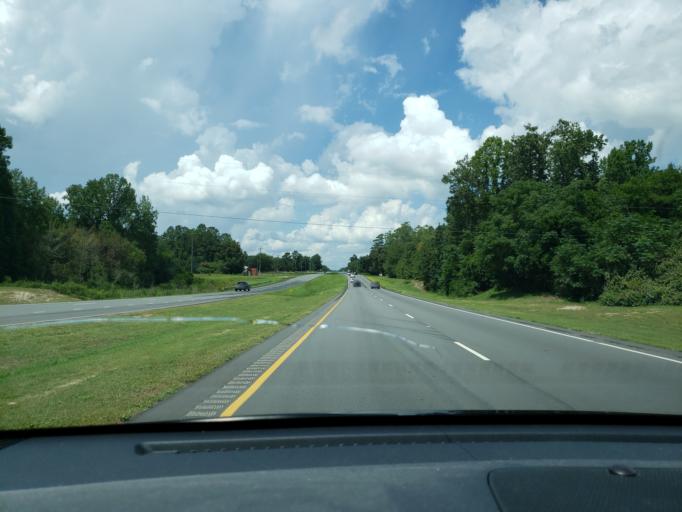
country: US
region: North Carolina
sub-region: Robeson County
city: Saint Pauls
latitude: 34.8024
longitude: -78.8256
